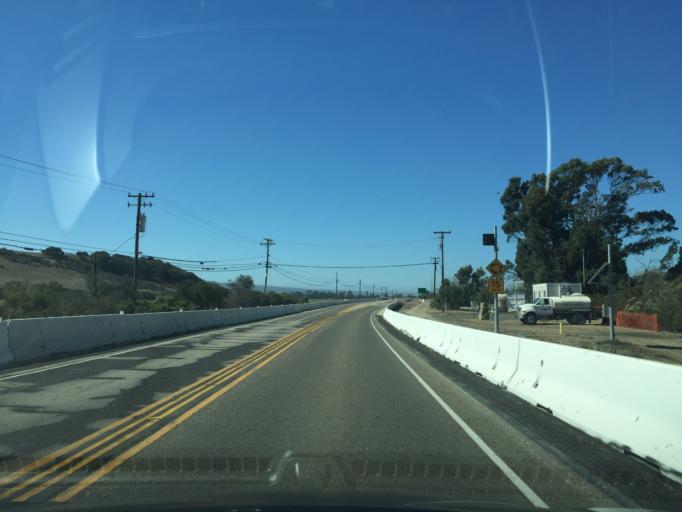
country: US
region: California
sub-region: Santa Barbara County
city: Mission Hills
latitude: 34.6646
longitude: -120.4026
